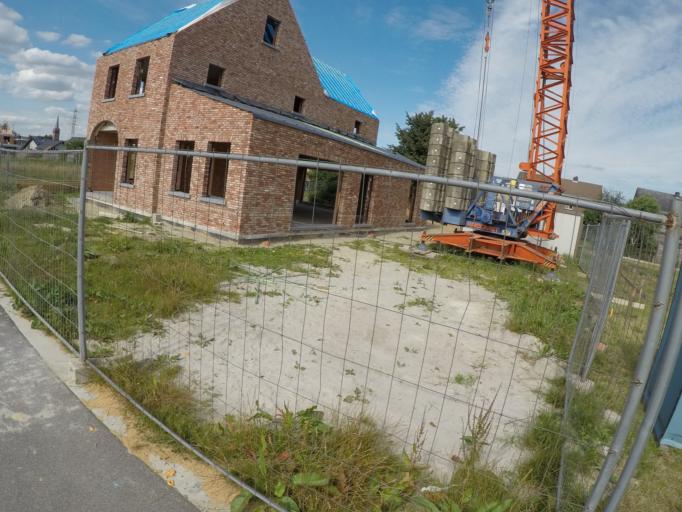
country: BE
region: Flanders
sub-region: Provincie Antwerpen
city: Lier
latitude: 51.1468
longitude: 4.6174
